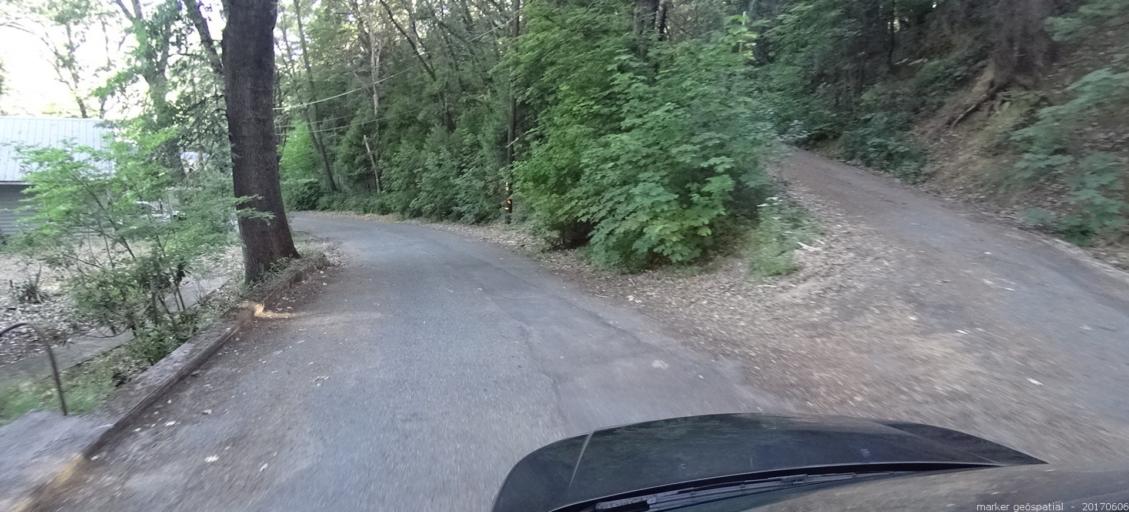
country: US
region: California
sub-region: Siskiyou County
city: Dunsmuir
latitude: 41.2005
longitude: -122.2710
